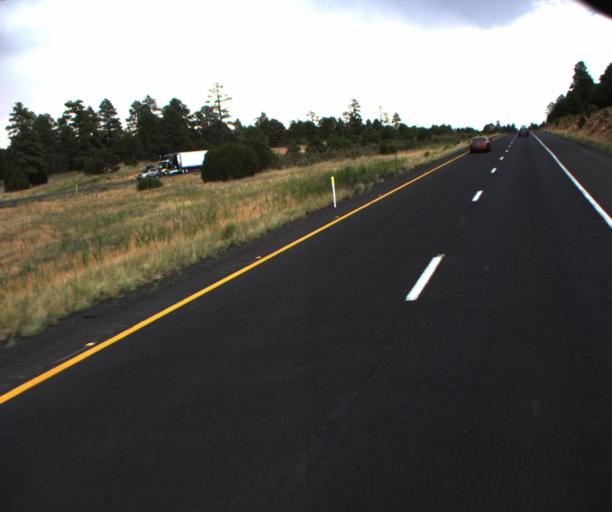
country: US
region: Arizona
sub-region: Coconino County
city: Flagstaff
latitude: 35.2124
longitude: -111.5343
